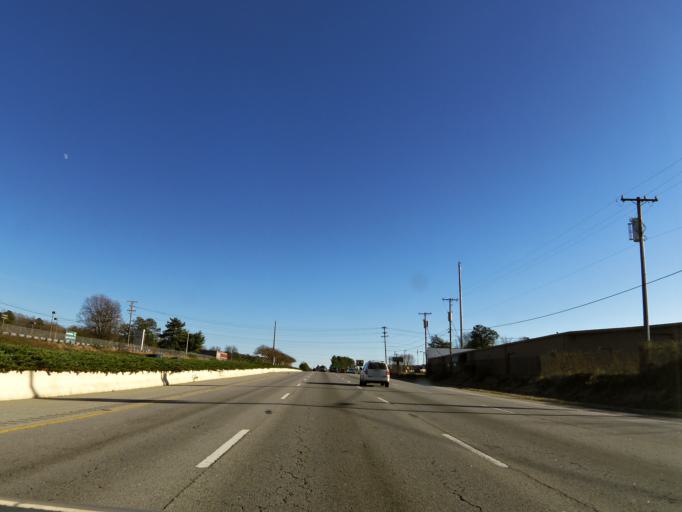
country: US
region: South Carolina
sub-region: Greenville County
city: Wade Hampton
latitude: 34.8439
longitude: -82.3198
